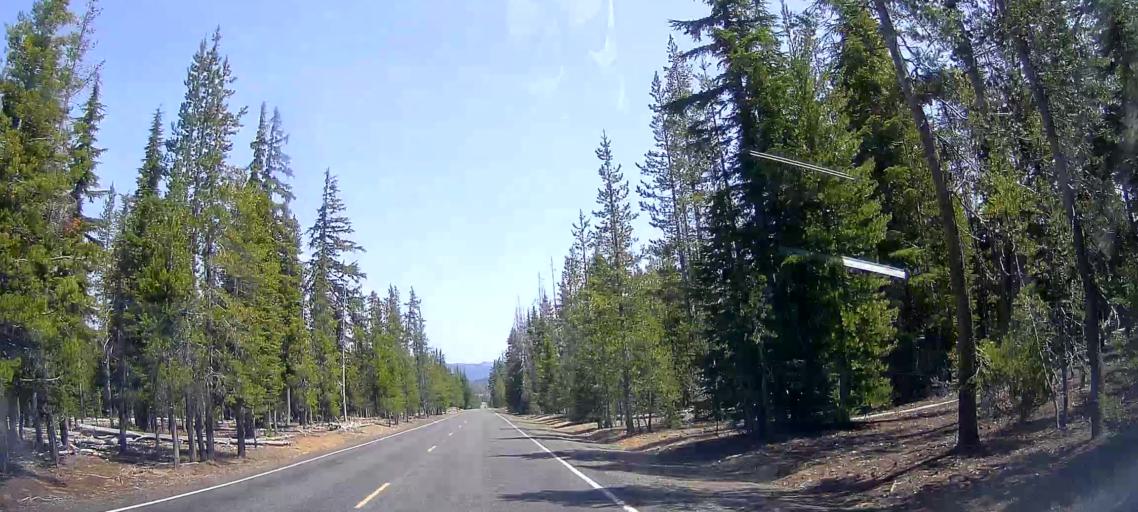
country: US
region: Oregon
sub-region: Jackson County
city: Shady Cove
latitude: 43.0113
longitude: -122.1298
